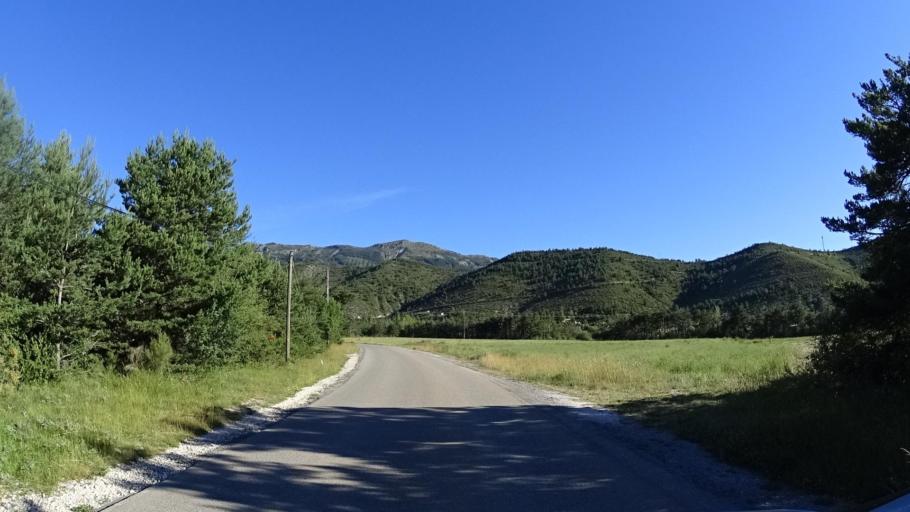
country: FR
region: Provence-Alpes-Cote d'Azur
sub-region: Departement des Alpes-de-Haute-Provence
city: Castellane
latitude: 43.8732
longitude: 6.5107
